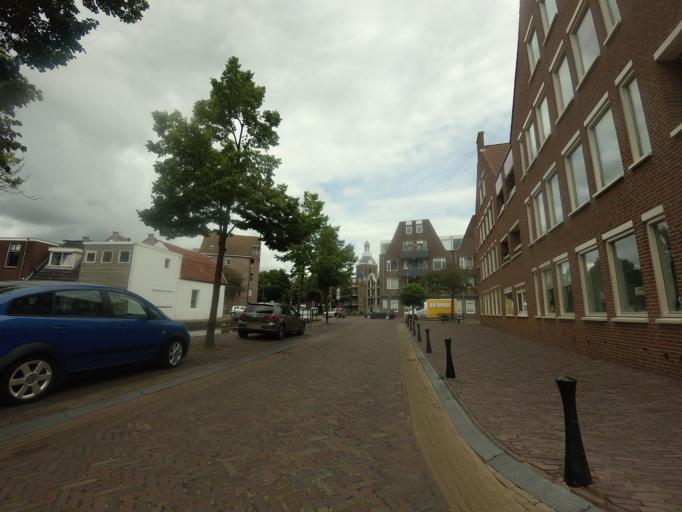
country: NL
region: Drenthe
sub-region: Gemeente Meppel
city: Meppel
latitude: 52.6960
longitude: 6.1882
